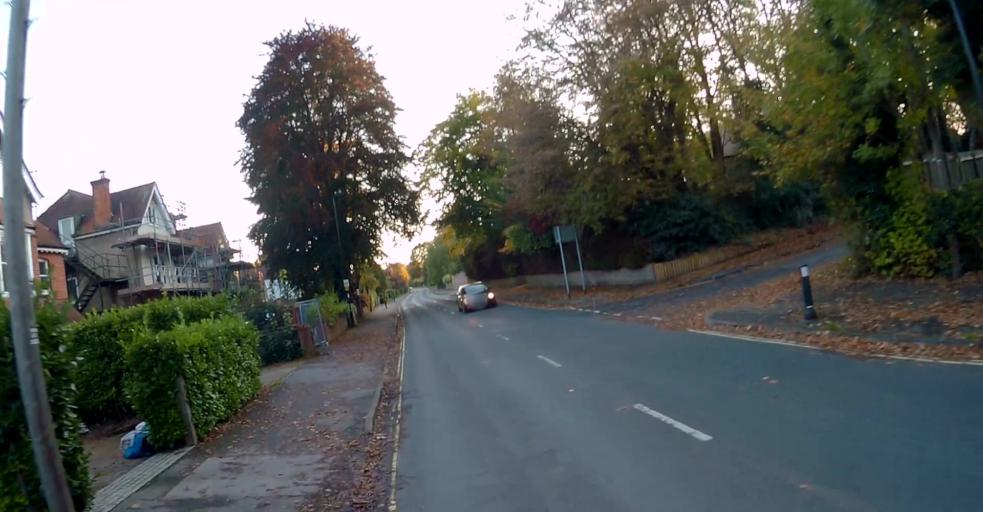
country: GB
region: England
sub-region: Hampshire
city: Basingstoke
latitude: 51.2551
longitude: -1.0861
